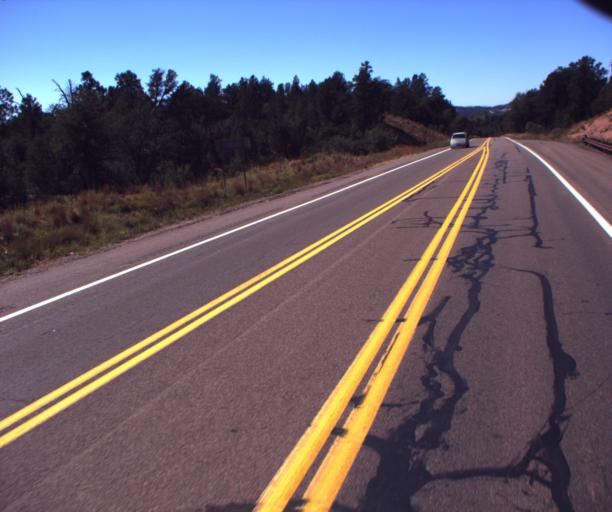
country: US
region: Arizona
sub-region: Gila County
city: Star Valley
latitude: 34.2633
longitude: -111.2425
